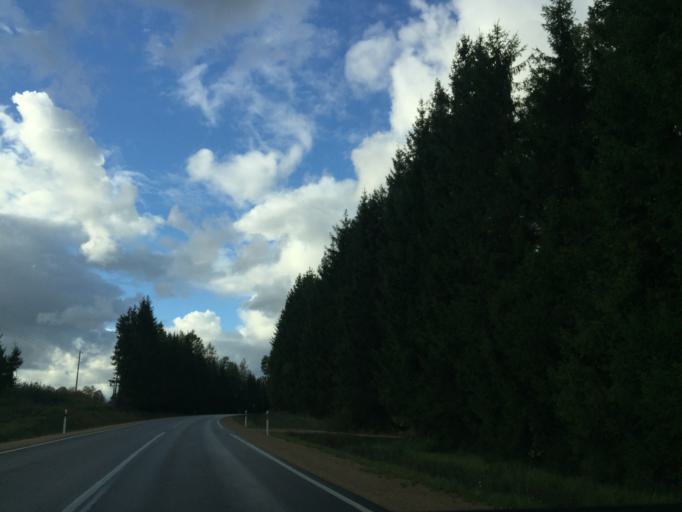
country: LV
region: Ligatne
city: Ligatne
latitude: 57.1644
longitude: 25.0506
